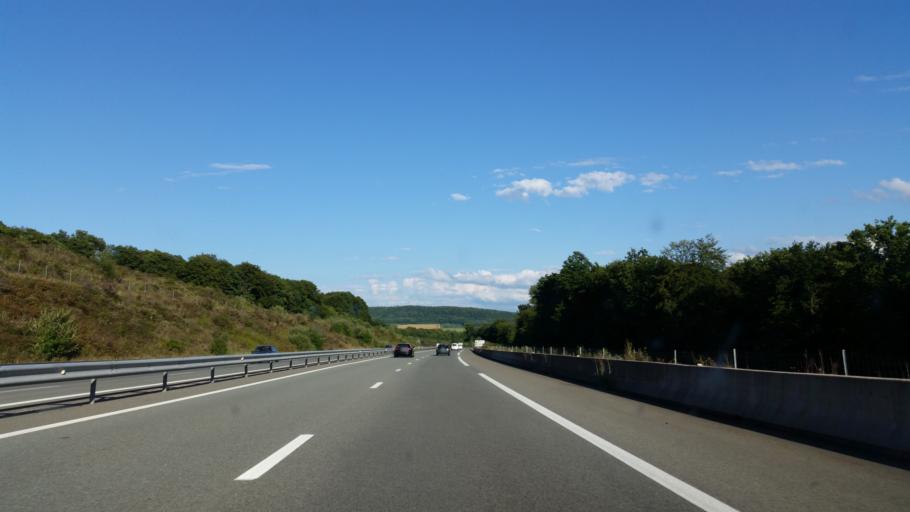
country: FR
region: Franche-Comte
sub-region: Departement de la Haute-Saone
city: Hericourt
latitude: 47.6078
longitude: 6.7013
